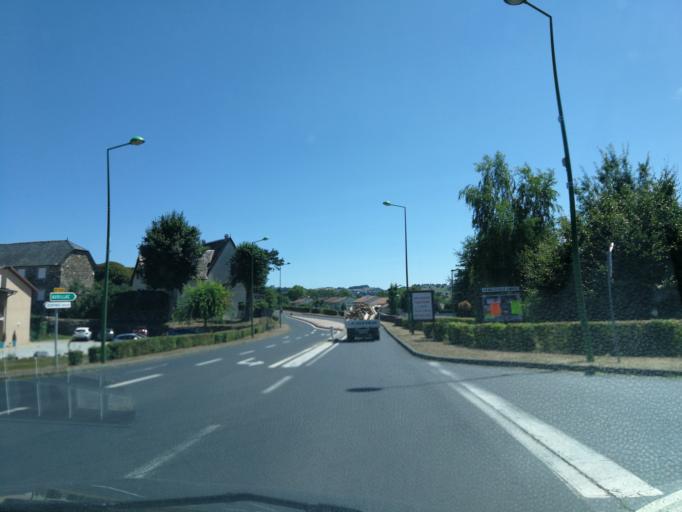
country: FR
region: Auvergne
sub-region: Departement du Cantal
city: Ytrac
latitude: 44.9333
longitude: 2.3804
